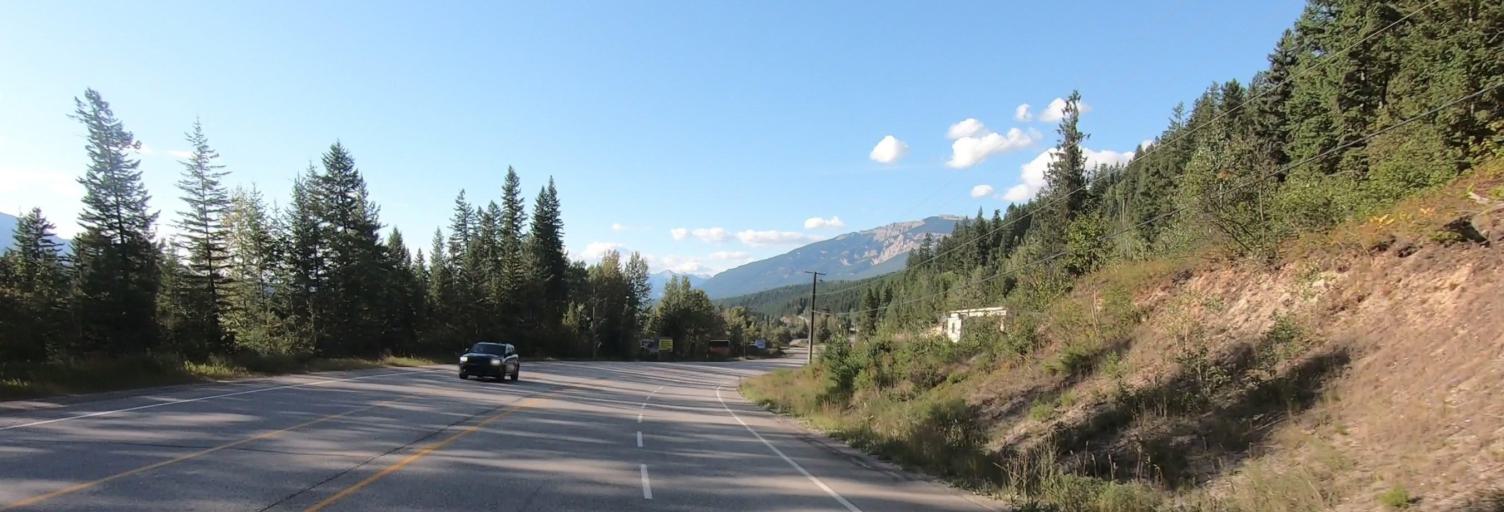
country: CA
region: British Columbia
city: Golden
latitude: 51.3839
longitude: -117.0243
